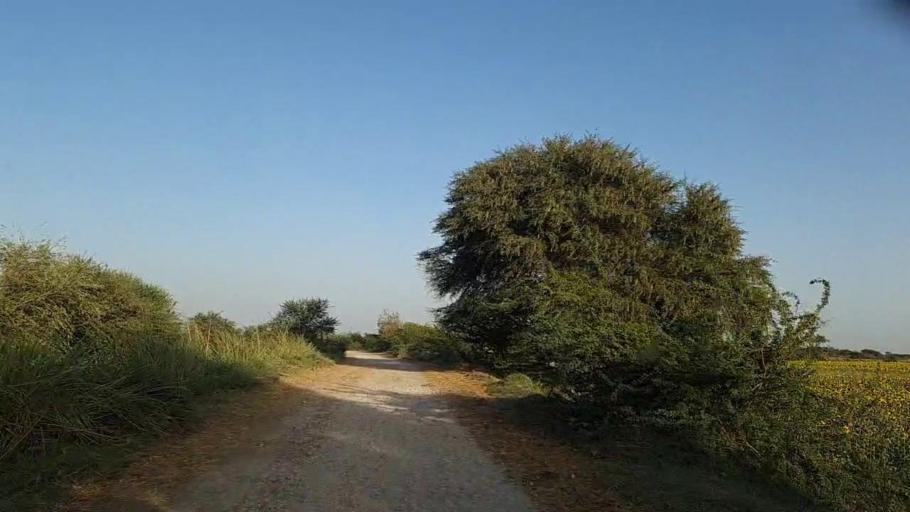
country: PK
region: Sindh
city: Jati
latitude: 24.4137
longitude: 68.3259
